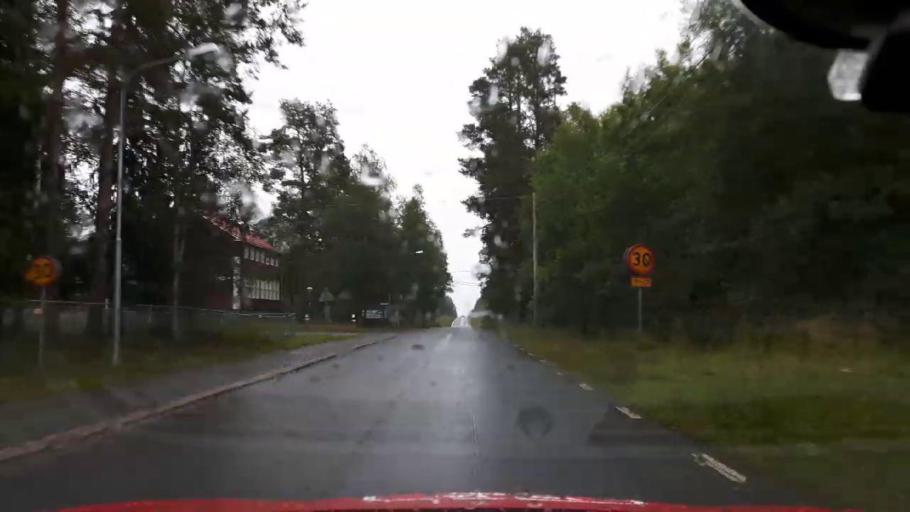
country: SE
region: Jaemtland
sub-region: OEstersunds Kommun
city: Brunflo
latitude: 63.0003
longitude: 14.7511
